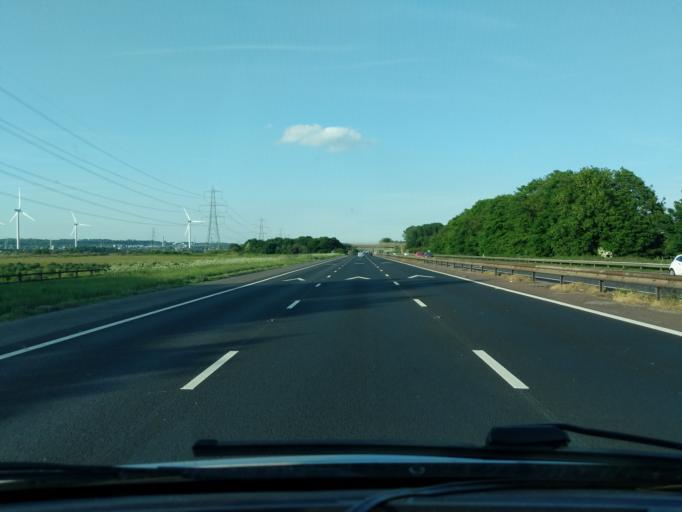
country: GB
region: England
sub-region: Cheshire West and Chester
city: Helsby
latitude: 53.2880
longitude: -2.7518
